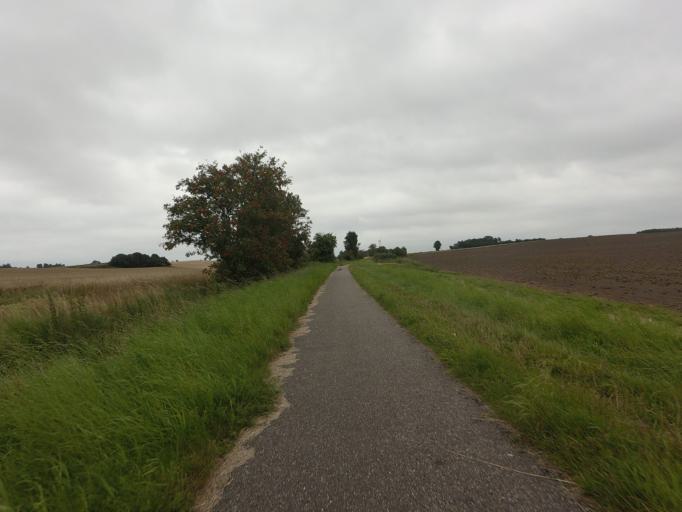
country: DK
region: Central Jutland
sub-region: Horsens Kommune
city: Braedstrup
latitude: 56.0214
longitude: 9.5764
